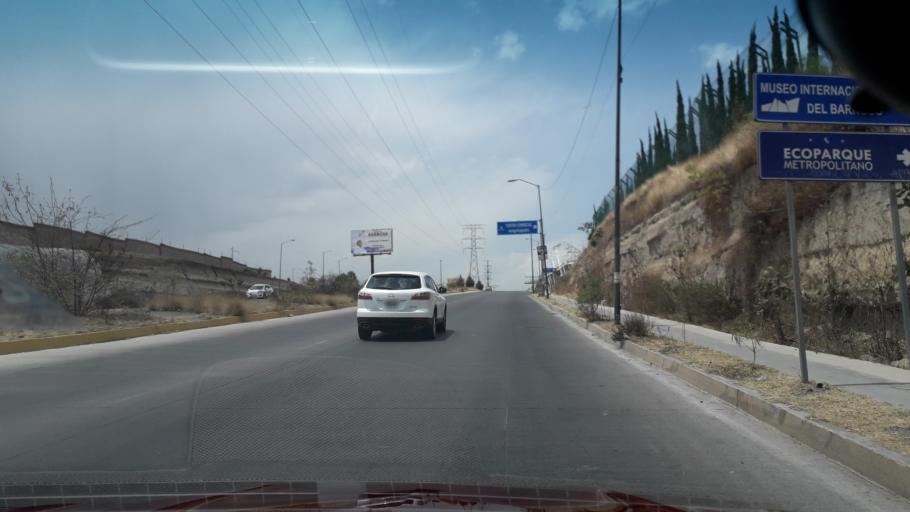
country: MX
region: Puebla
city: Tlazcalancingo
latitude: 19.0155
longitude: -98.2474
